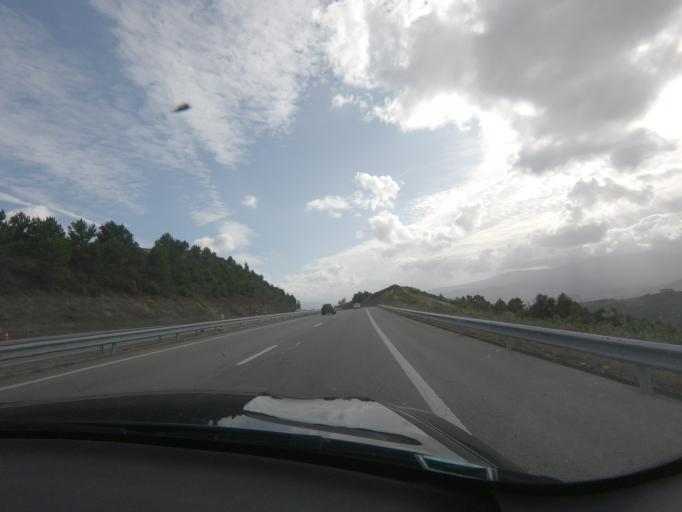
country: PT
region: Vila Real
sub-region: Vila Real
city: Vila Real
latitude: 41.2497
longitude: -7.7172
